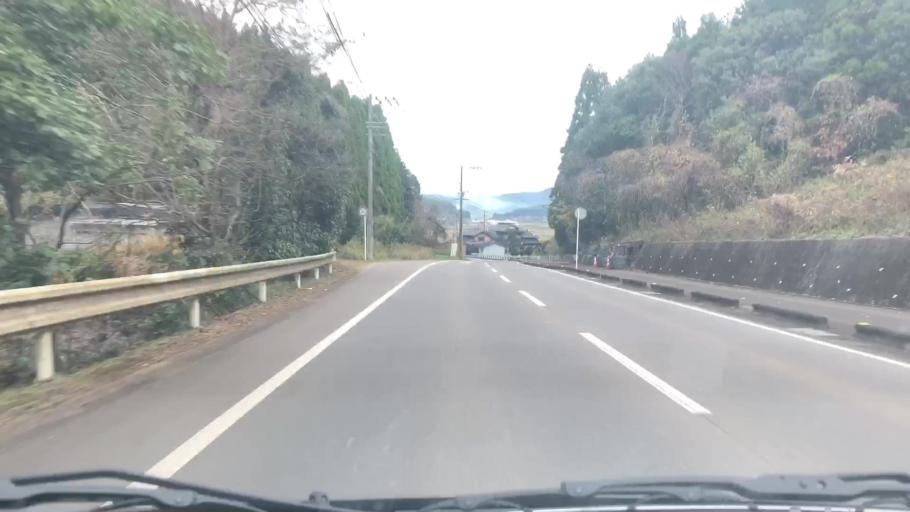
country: JP
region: Saga Prefecture
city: Takeocho-takeo
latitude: 33.2104
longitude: 129.9630
